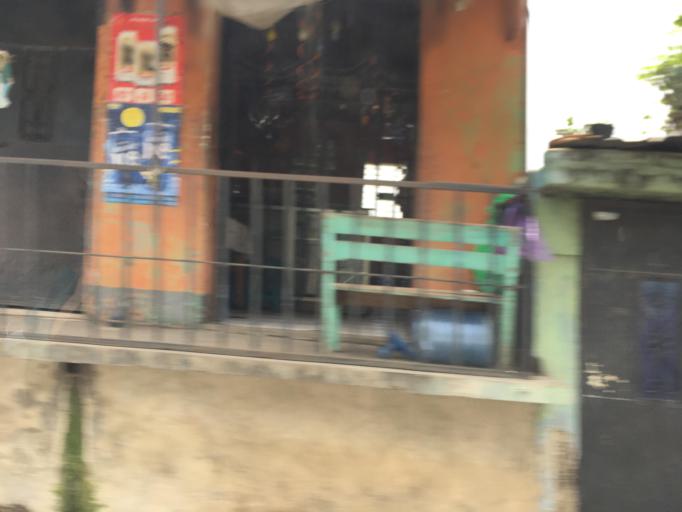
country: GT
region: Guatemala
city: Villa Canales
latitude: 14.4537
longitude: -90.5699
